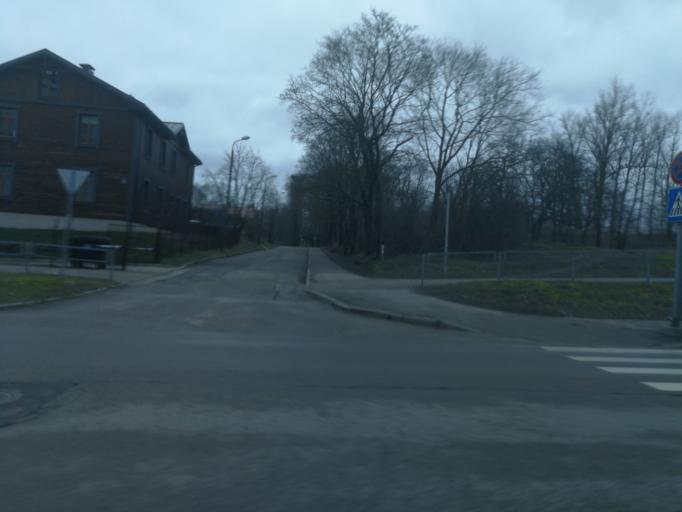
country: LV
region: Riga
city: Bolderaja
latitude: 57.0348
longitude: 24.1014
